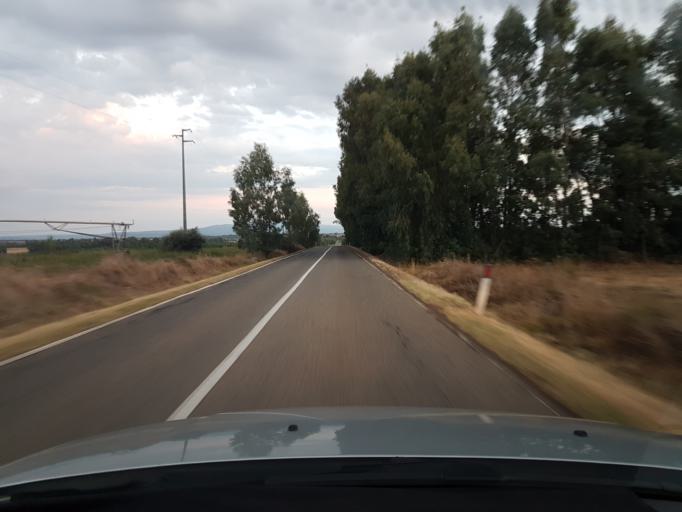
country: IT
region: Sardinia
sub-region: Provincia di Oristano
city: Tramatza
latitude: 40.0215
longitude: 8.6424
